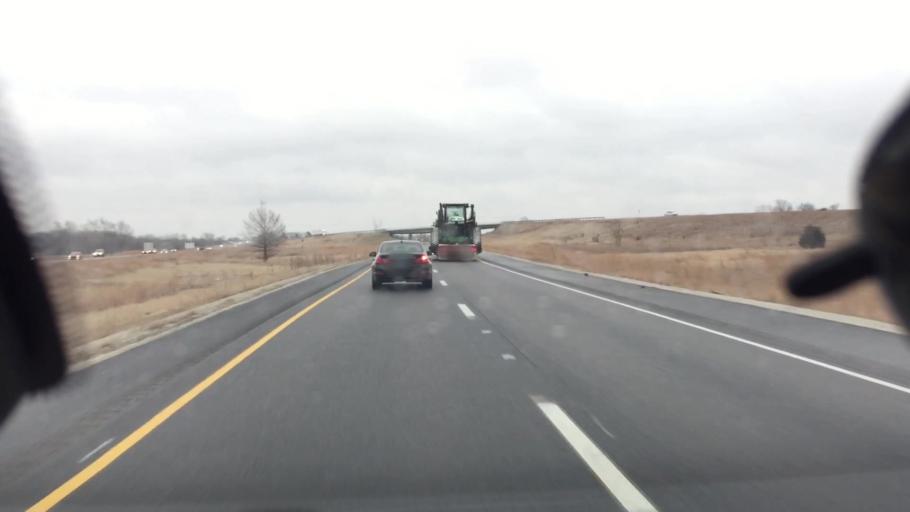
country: US
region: Illinois
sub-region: Tazewell County
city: East Peoria
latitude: 40.6348
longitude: -89.5228
